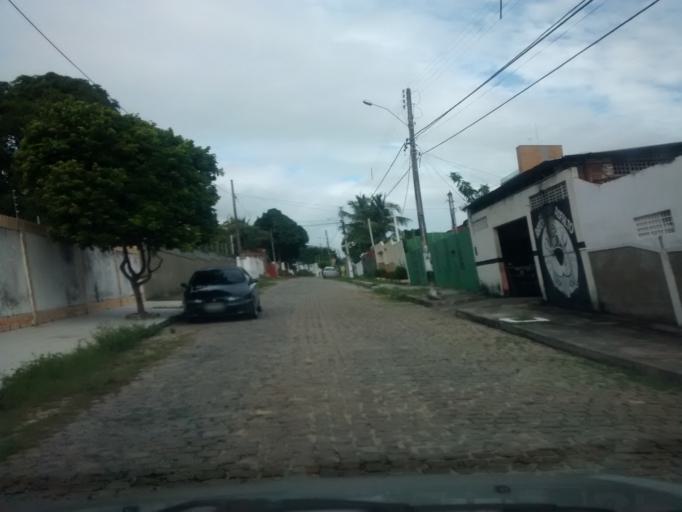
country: BR
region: Rio Grande do Norte
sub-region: Natal
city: Natal
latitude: -5.8732
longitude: -35.1832
